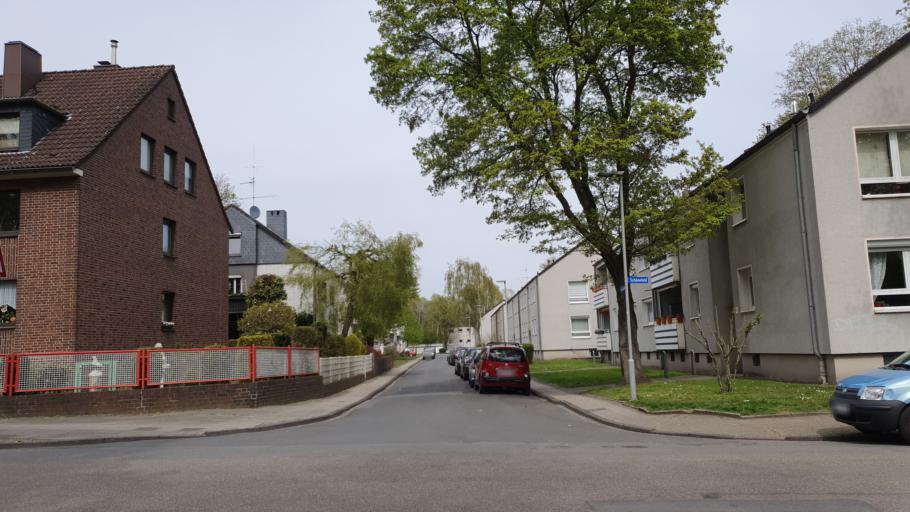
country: DE
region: North Rhine-Westphalia
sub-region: Regierungsbezirk Dusseldorf
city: Oberhausen
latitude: 51.4610
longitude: 6.8730
